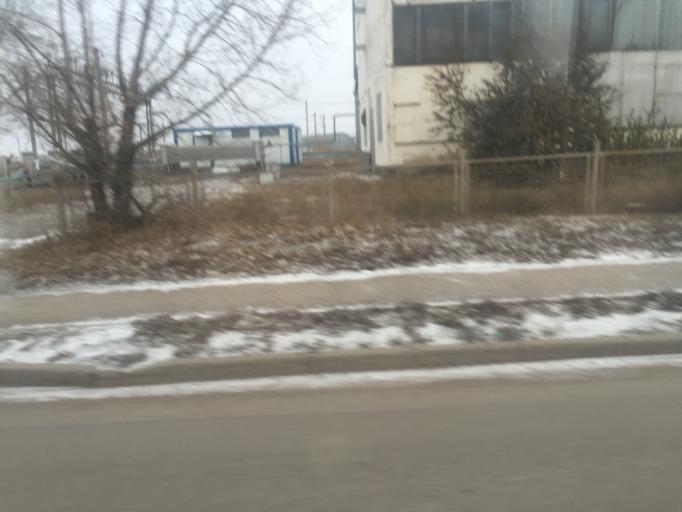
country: KZ
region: Astana Qalasy
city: Astana
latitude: 51.2034
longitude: 71.3836
